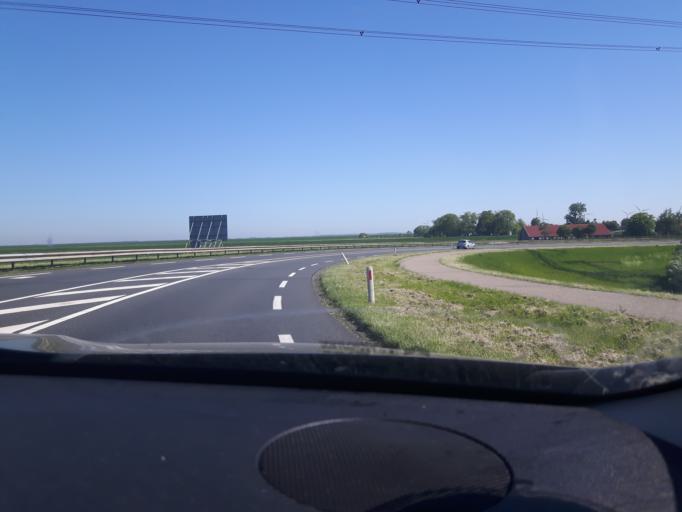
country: NL
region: Zeeland
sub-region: Gemeente Tholen
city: Tholen
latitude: 51.4258
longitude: 4.1874
